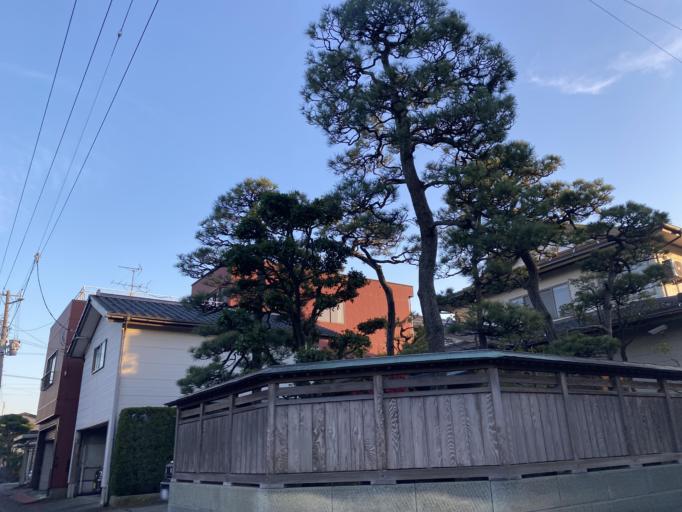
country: JP
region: Niigata
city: Kashiwazaki
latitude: 37.3743
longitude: 138.5637
